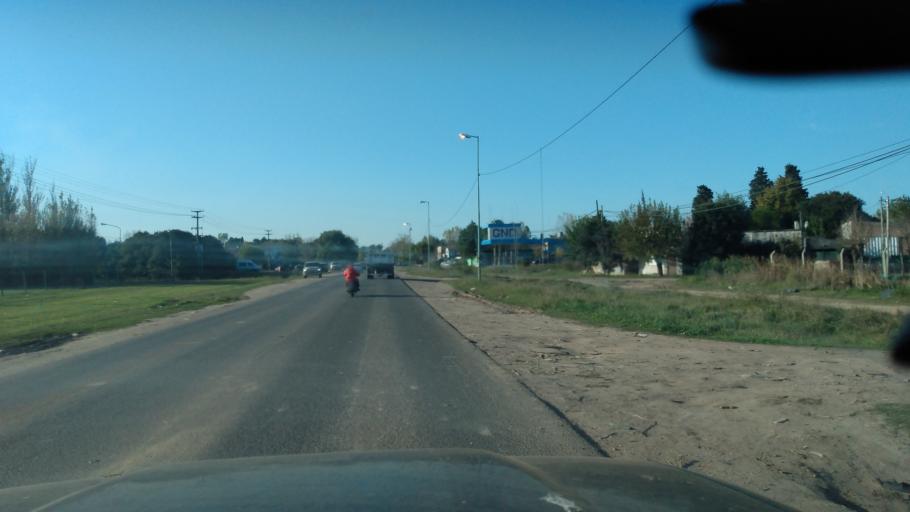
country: AR
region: Buenos Aires
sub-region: Partido de Lujan
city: Lujan
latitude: -34.5418
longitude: -59.1210
